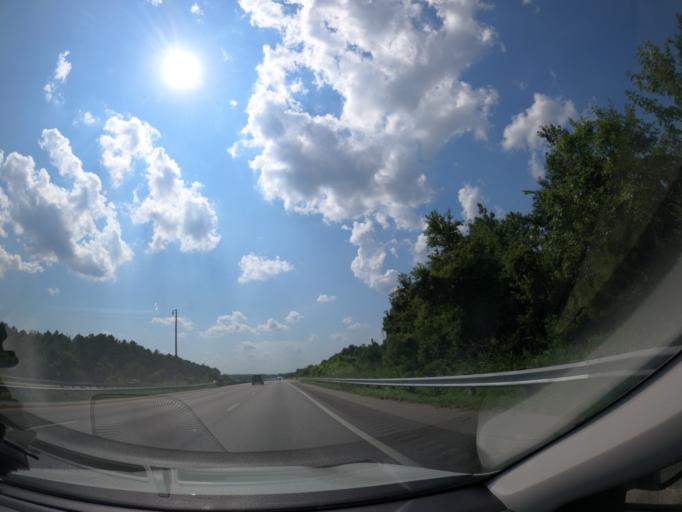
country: US
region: South Carolina
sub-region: Lexington County
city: Cayce
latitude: 33.9284
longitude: -81.0304
